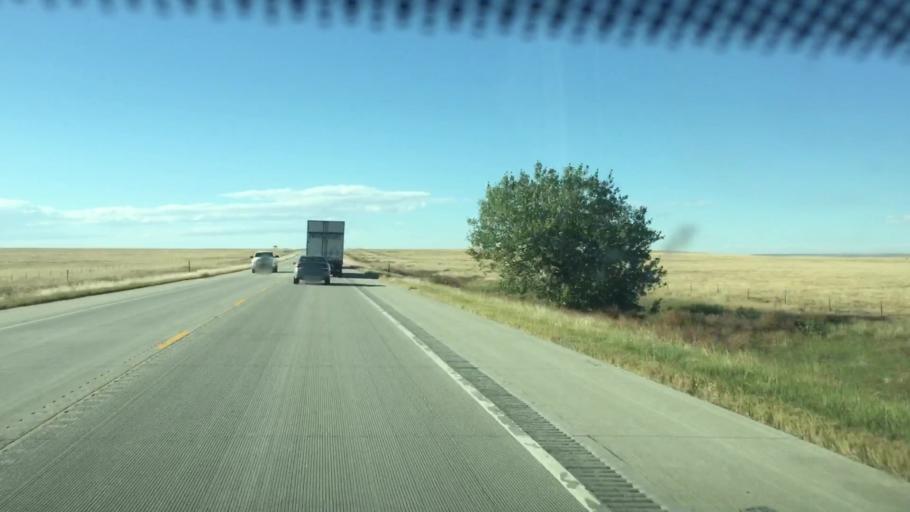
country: US
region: Colorado
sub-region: Lincoln County
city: Hugo
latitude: 38.9193
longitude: -103.1834
